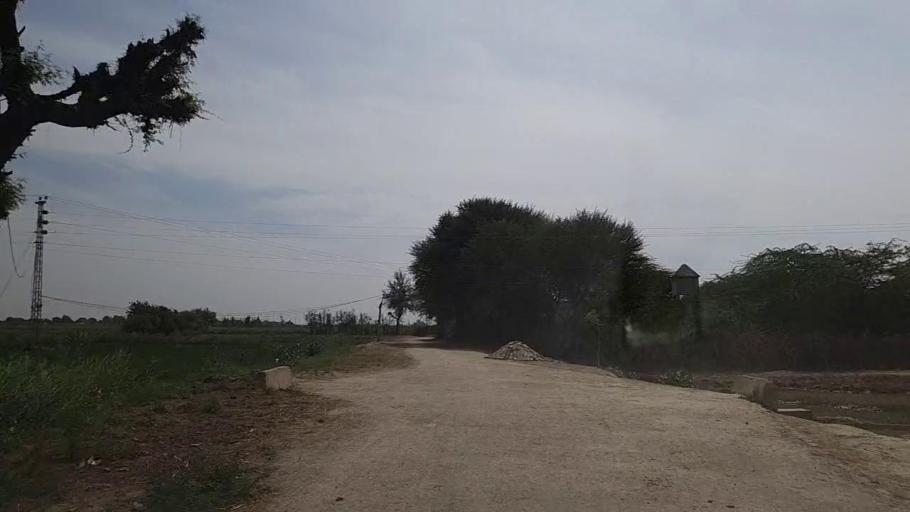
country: PK
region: Sindh
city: Kunri
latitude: 25.2100
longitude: 69.4930
